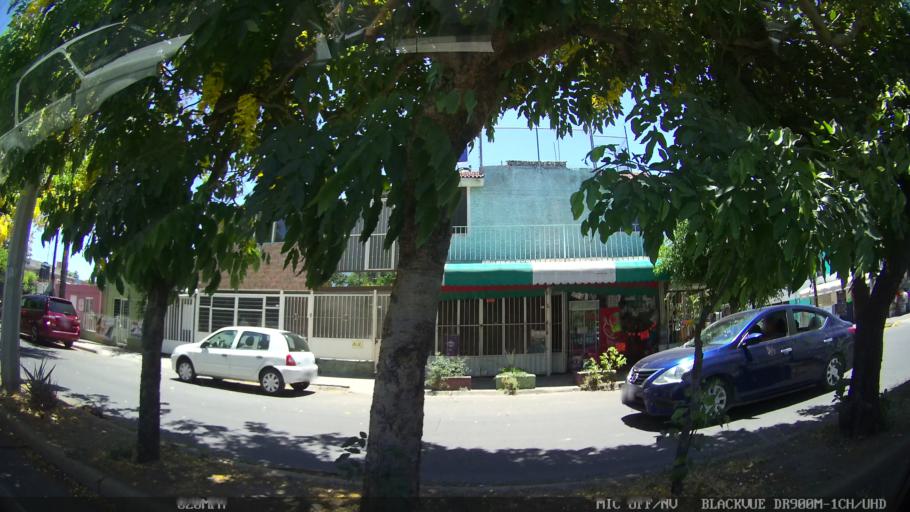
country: MX
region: Jalisco
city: Tlaquepaque
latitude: 20.6623
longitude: -103.2813
